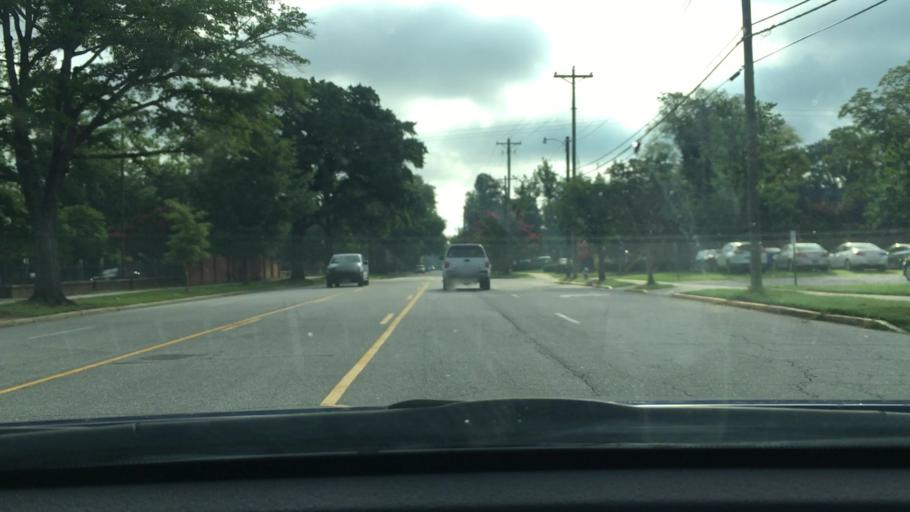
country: US
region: South Carolina
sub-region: Richland County
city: Columbia
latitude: 34.0137
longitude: -81.0325
